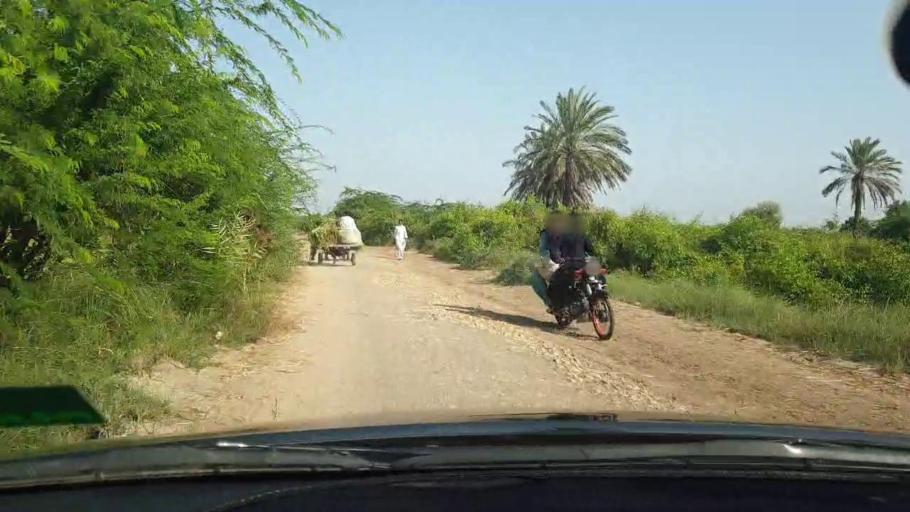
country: PK
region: Sindh
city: Tando Bago
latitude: 24.7176
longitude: 68.9913
